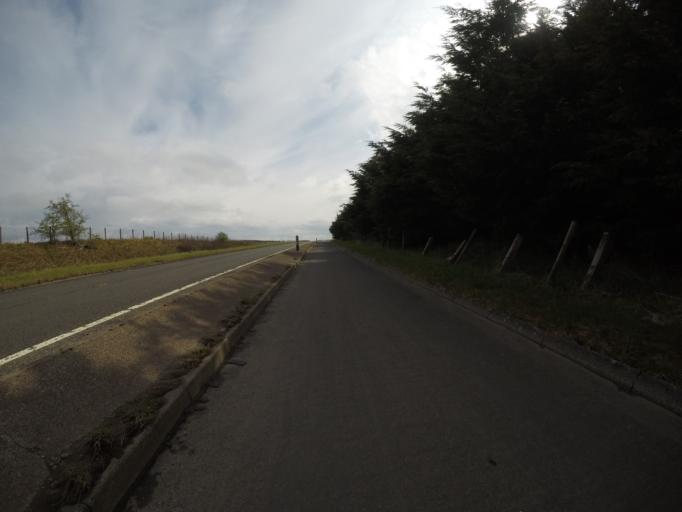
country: GB
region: Scotland
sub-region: East Renfrewshire
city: Newton Mearns
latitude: 55.7317
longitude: -4.3820
